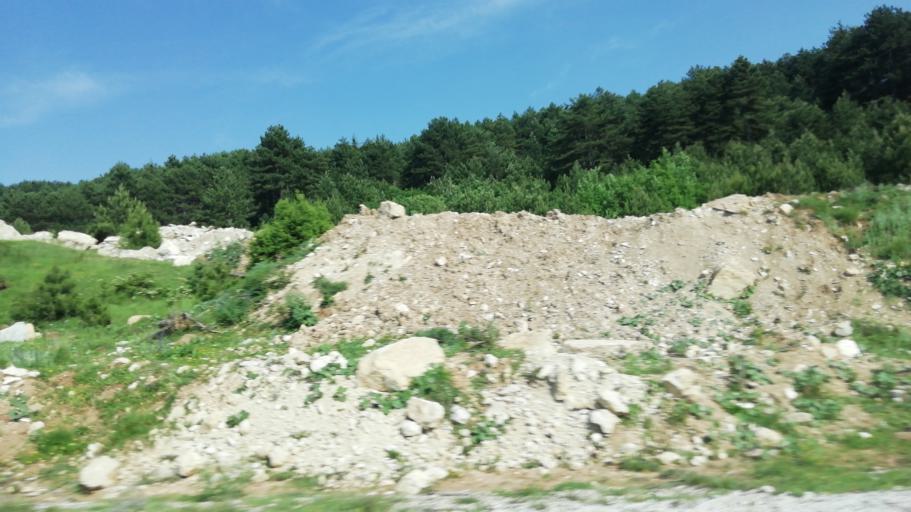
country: TR
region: Karabuk
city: Karabuk
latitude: 41.1178
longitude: 32.5800
